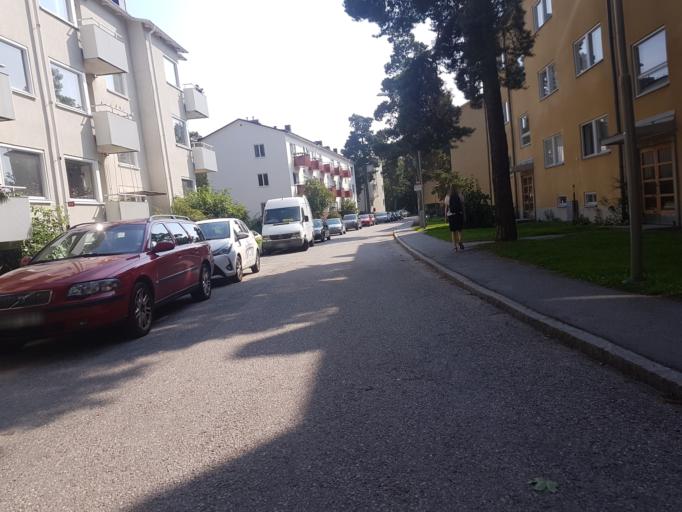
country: SE
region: Stockholm
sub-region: Stockholms Kommun
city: OEstermalm
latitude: 59.2964
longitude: 18.1033
